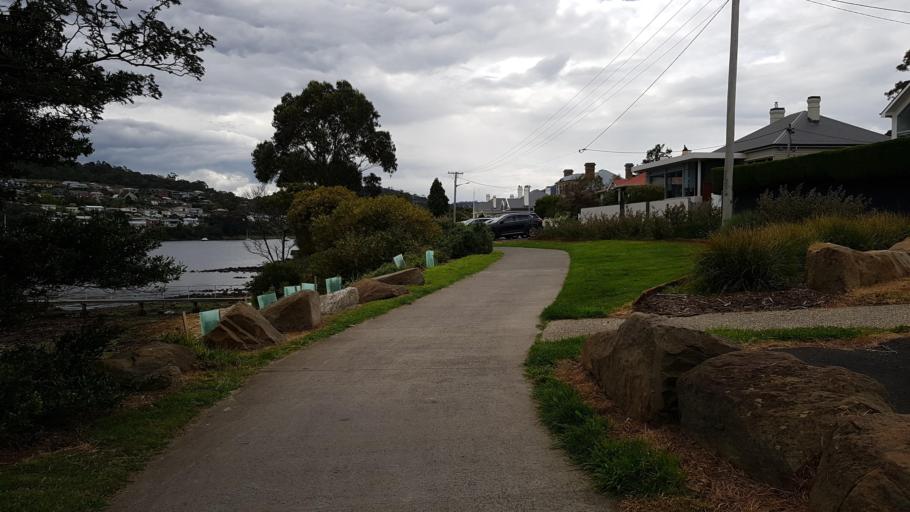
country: AU
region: Tasmania
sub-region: Clarence
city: Bellerive
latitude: -42.8777
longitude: 147.3634
